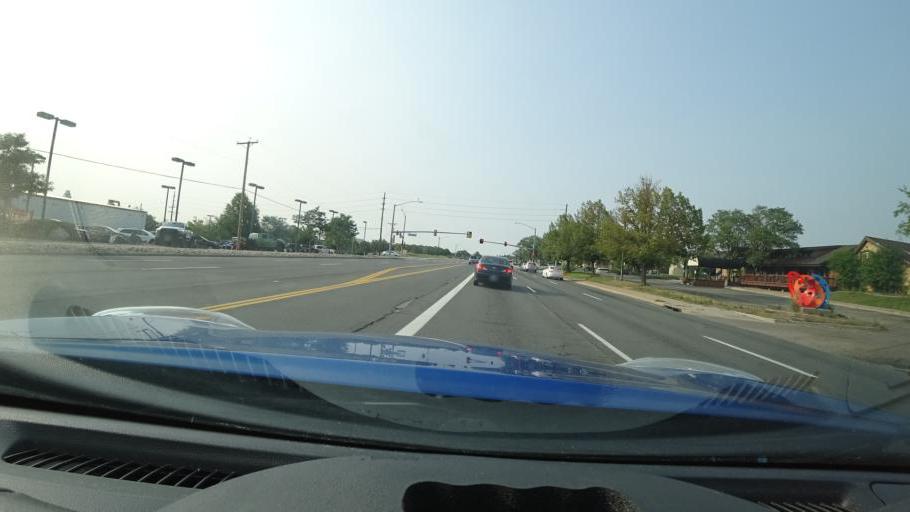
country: US
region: Colorado
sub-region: Adams County
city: Aurora
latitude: 39.6666
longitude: -104.8661
